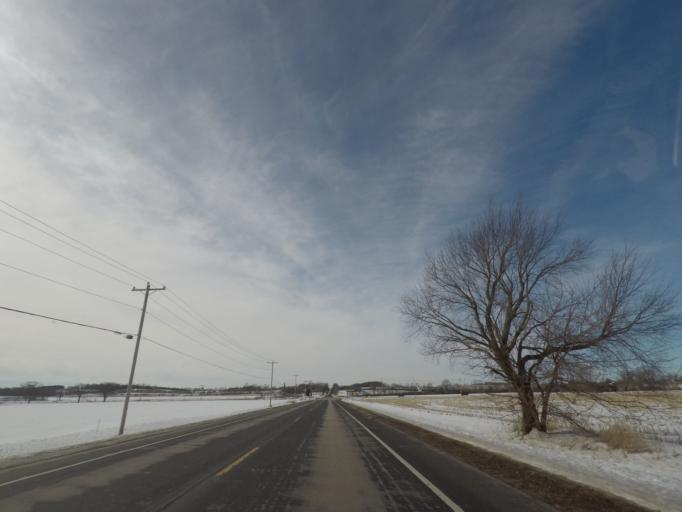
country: US
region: Wisconsin
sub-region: Dane County
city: Fitchburg
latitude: 43.0012
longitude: -89.4561
